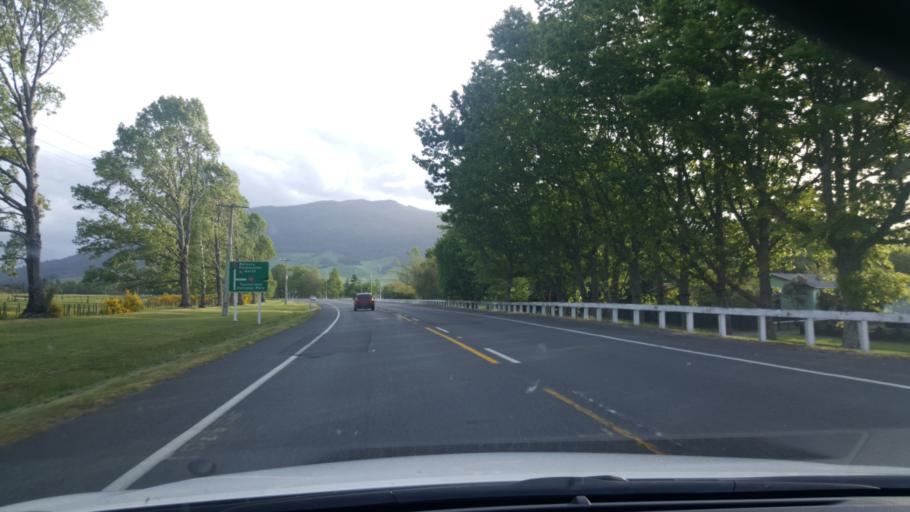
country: NZ
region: Waikato
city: Turangi
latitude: -38.9942
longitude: 175.8065
